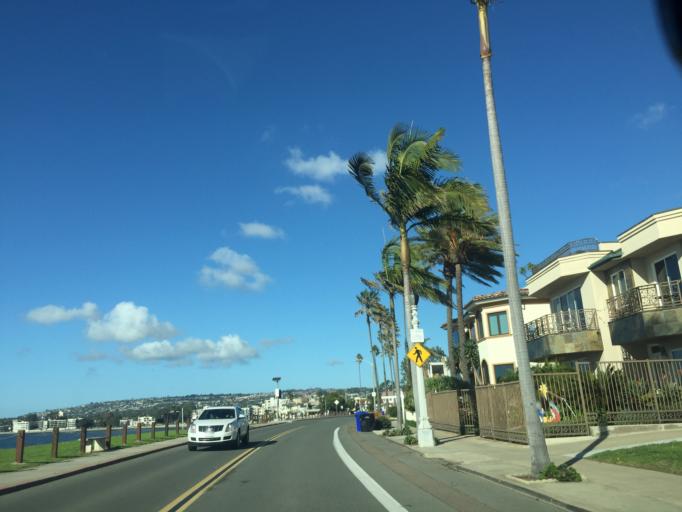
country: US
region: California
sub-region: San Diego County
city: La Jolla
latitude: 32.7837
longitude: -117.2394
